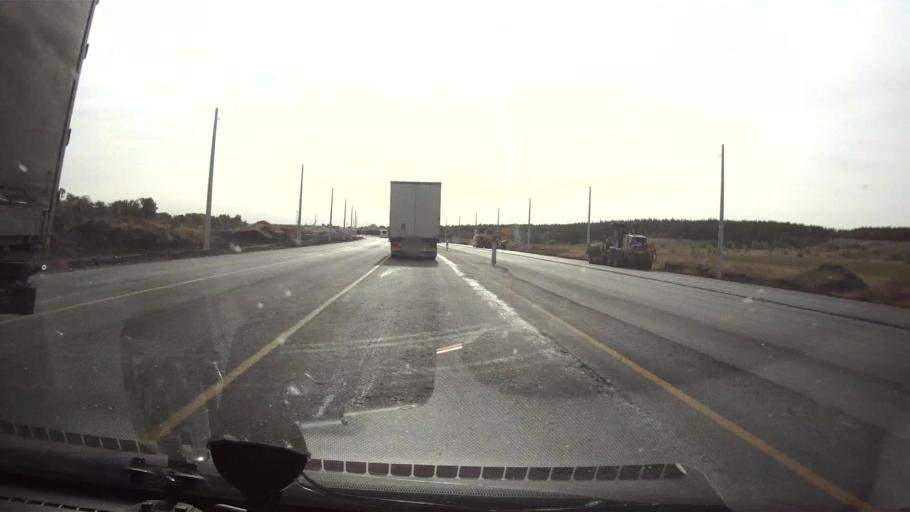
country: RU
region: Saratov
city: Sinodskoye
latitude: 52.0181
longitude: 46.7002
